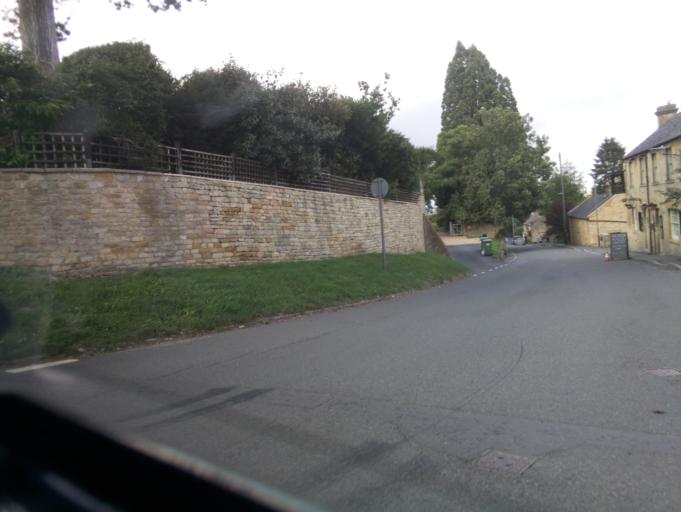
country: GB
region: England
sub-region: Gloucestershire
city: Chipping Campden
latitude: 52.0137
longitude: -1.7599
